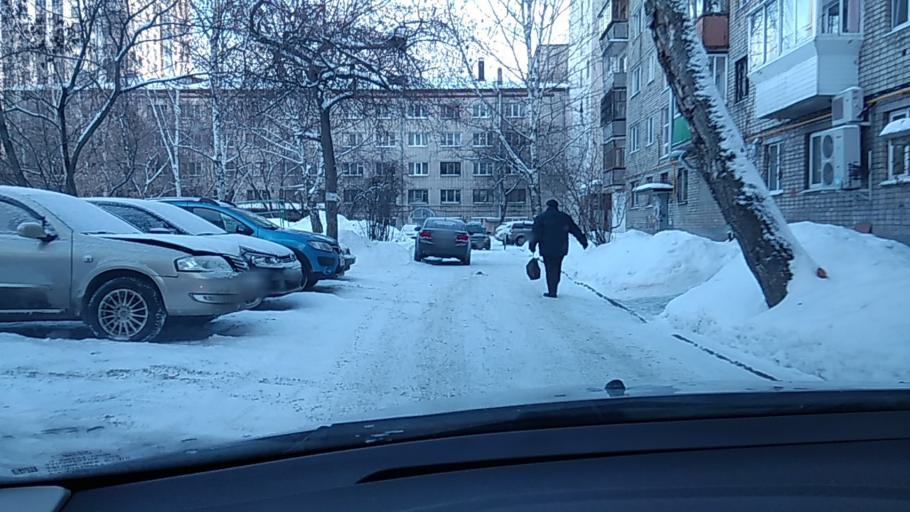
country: RU
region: Sverdlovsk
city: Yekaterinburg
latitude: 56.8098
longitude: 60.6180
